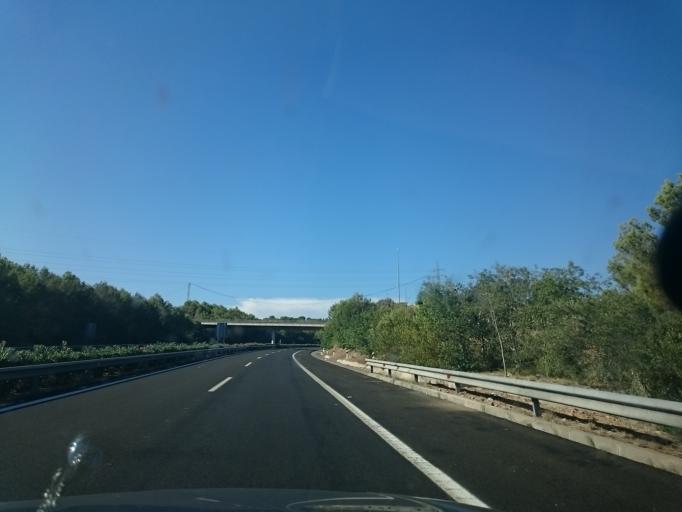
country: ES
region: Catalonia
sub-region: Provincia de Barcelona
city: Cubelles
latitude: 41.2365
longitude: 1.6820
